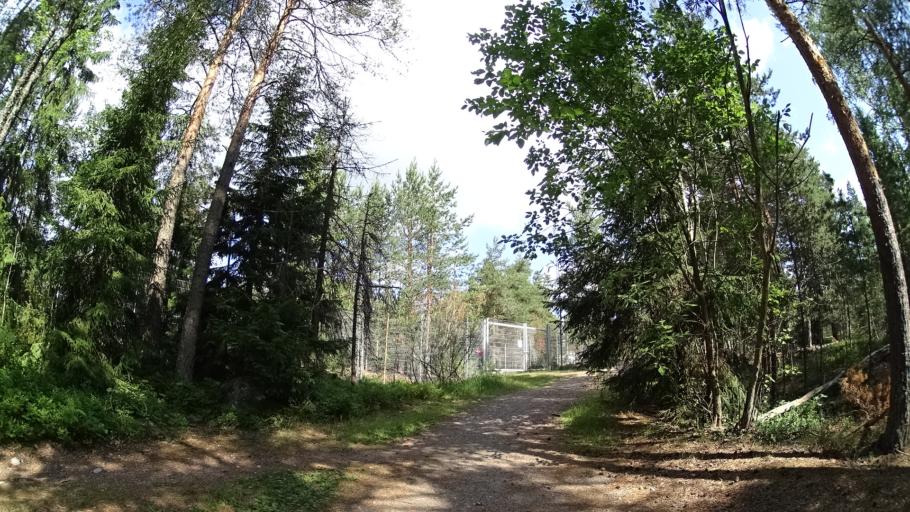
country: FI
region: Uusimaa
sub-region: Helsinki
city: Teekkarikylae
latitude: 60.2762
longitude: 24.9010
